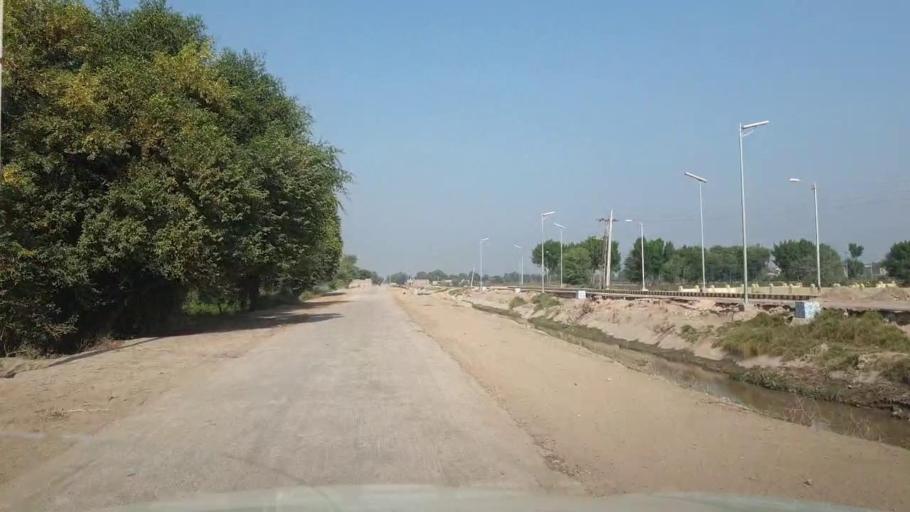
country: PK
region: Sindh
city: Bhan
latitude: 26.5378
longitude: 67.7755
